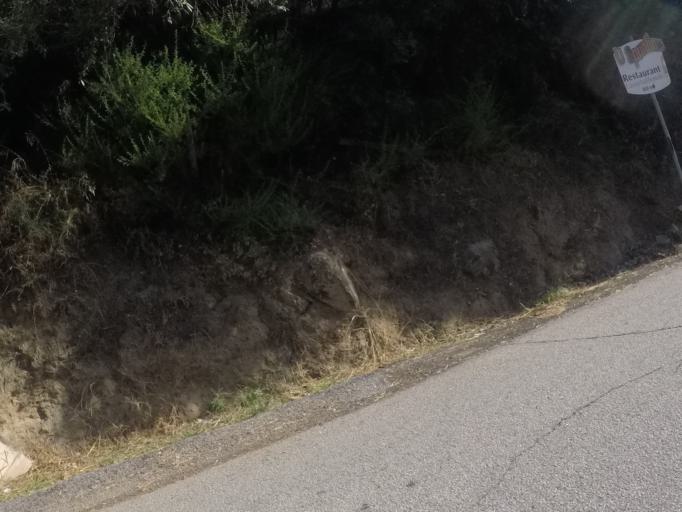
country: FR
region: Corsica
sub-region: Departement de la Corse-du-Sud
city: Olmeto
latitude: 41.7508
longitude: 8.9123
